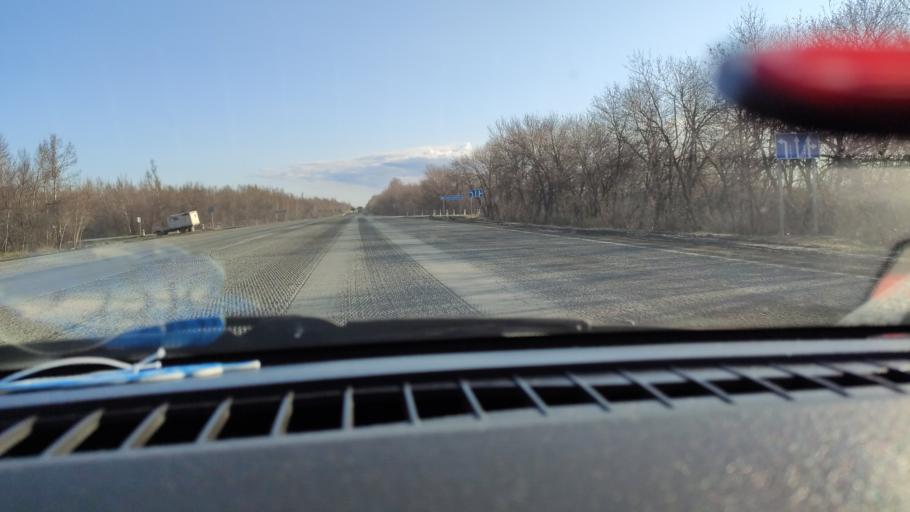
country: RU
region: Saratov
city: Dukhovnitskoye
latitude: 52.6637
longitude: 48.2140
